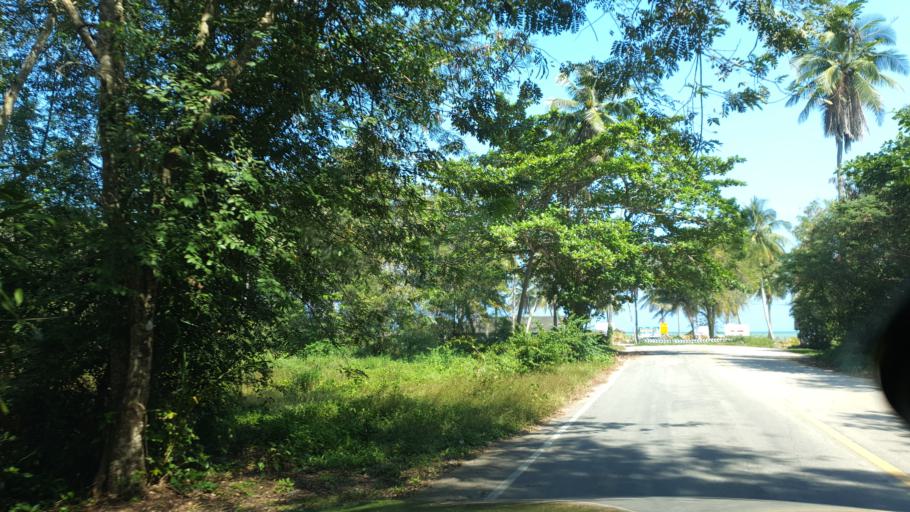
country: TH
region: Surat Thani
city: Tha Chana
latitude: 9.5881
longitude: 99.2066
